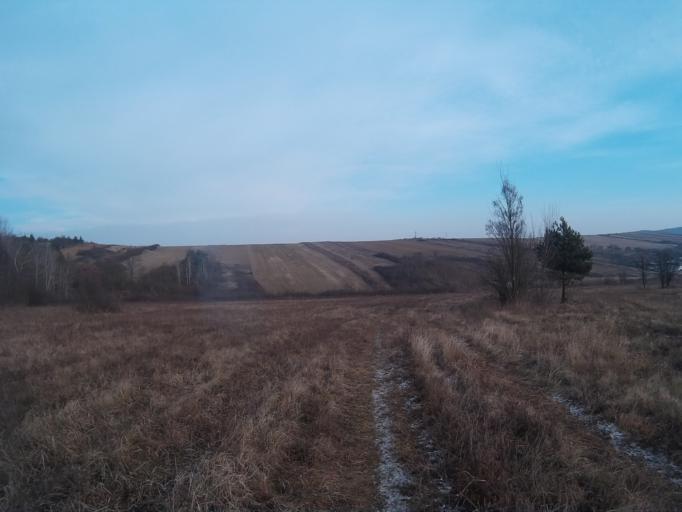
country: HU
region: Borsod-Abauj-Zemplen
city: Szendro
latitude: 48.4661
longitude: 20.8340
